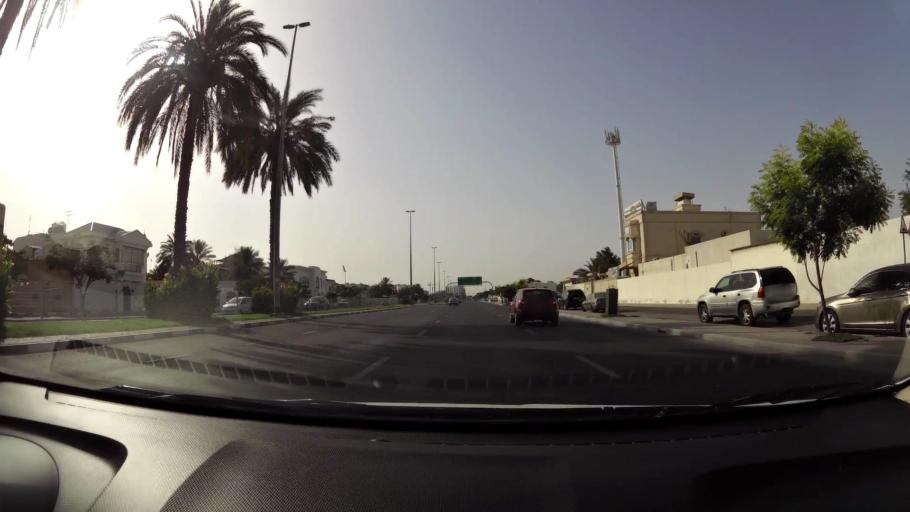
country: AE
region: Ash Shariqah
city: Sharjah
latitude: 25.2925
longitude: 55.3426
